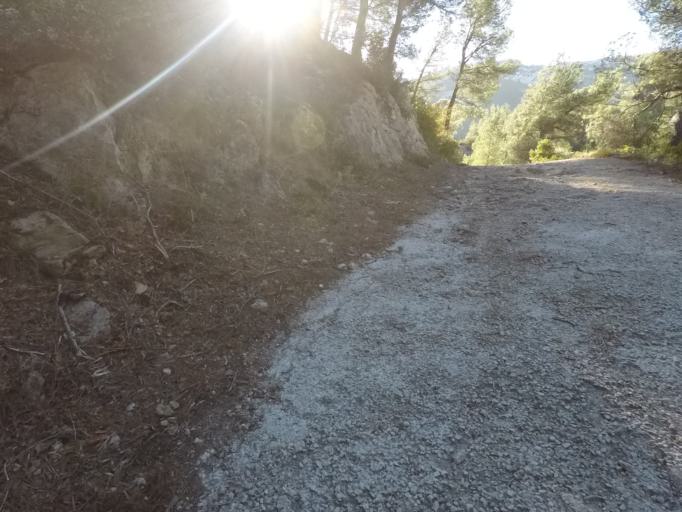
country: FR
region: Provence-Alpes-Cote d'Azur
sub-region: Departement des Bouches-du-Rhone
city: La Penne-sur-Huveaune
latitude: 43.2740
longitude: 5.4877
